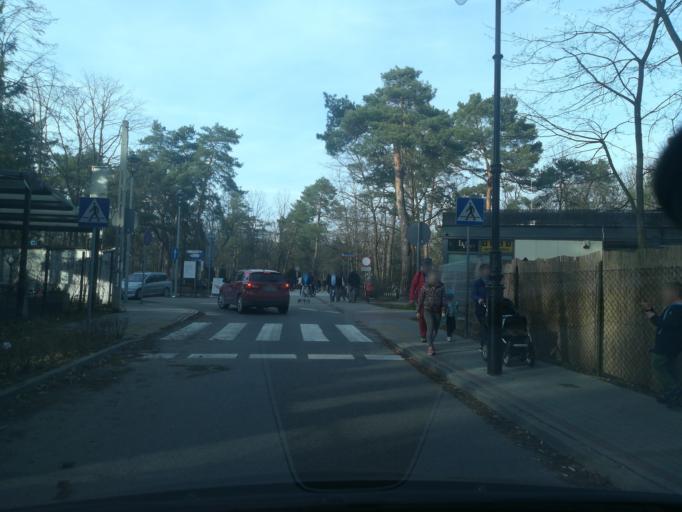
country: PL
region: Masovian Voivodeship
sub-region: Powiat piaseczynski
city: Konstancin-Jeziorna
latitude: 52.0839
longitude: 21.1168
